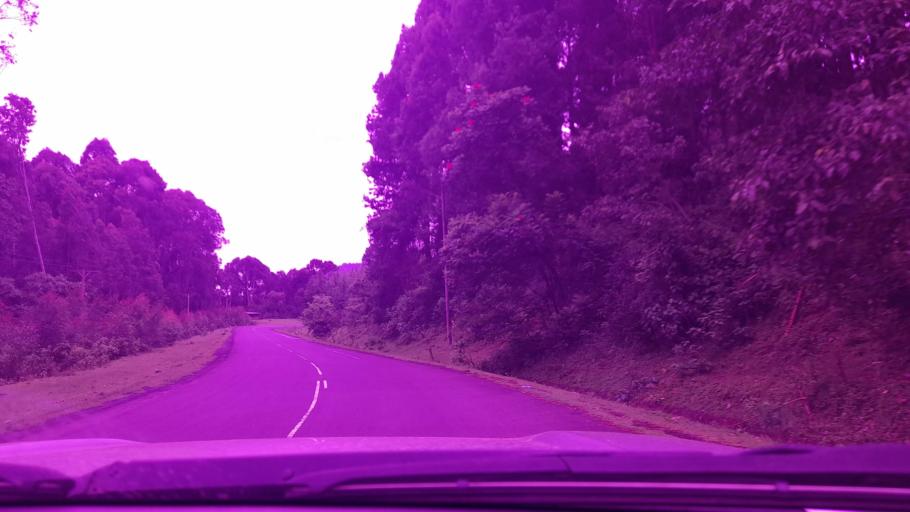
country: ET
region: Oromiya
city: Jima
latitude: 7.5561
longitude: 36.5867
